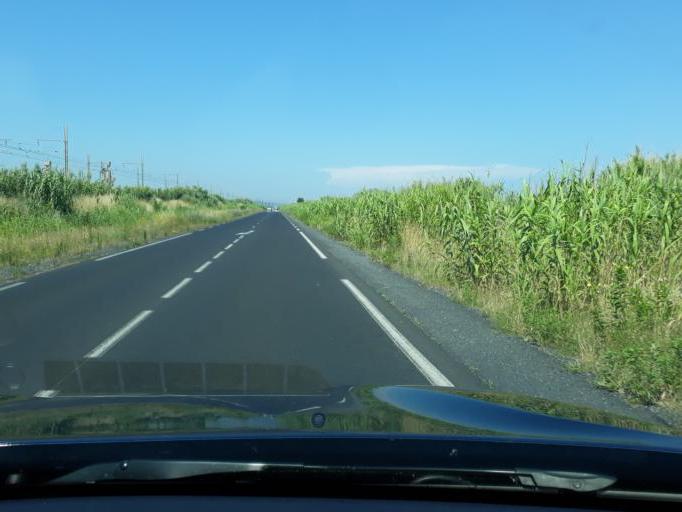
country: FR
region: Languedoc-Roussillon
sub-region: Departement de l'Herault
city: Marseillan
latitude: 43.3437
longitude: 3.5792
